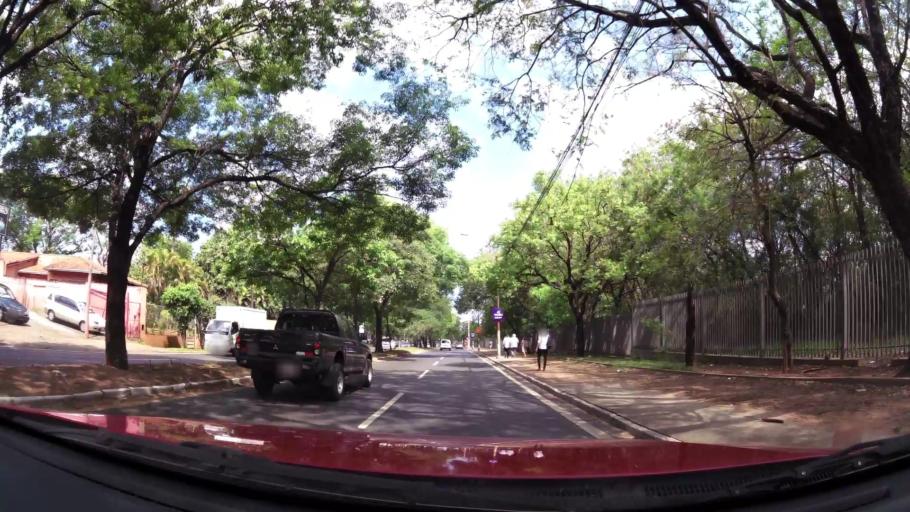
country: PY
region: Central
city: Fernando de la Mora
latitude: -25.3271
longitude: -57.5190
